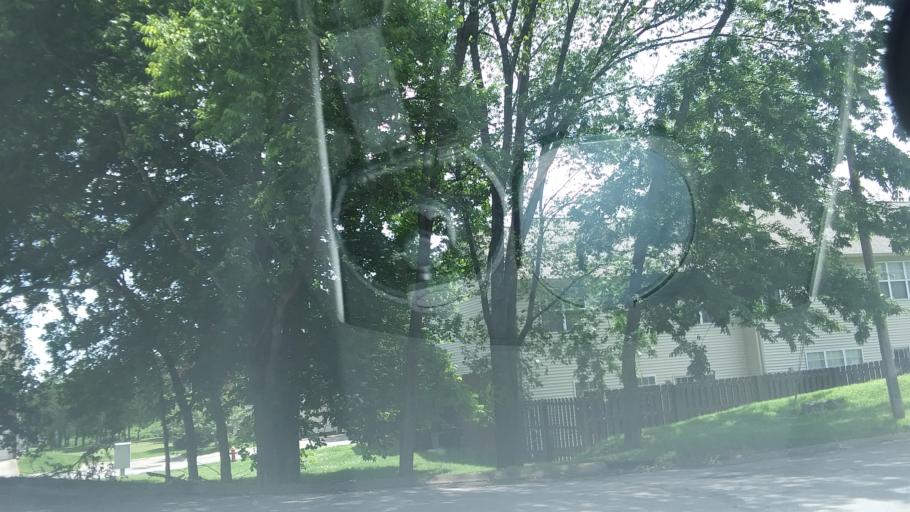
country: US
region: Tennessee
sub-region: Rutherford County
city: La Vergne
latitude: 36.0934
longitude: -86.6398
